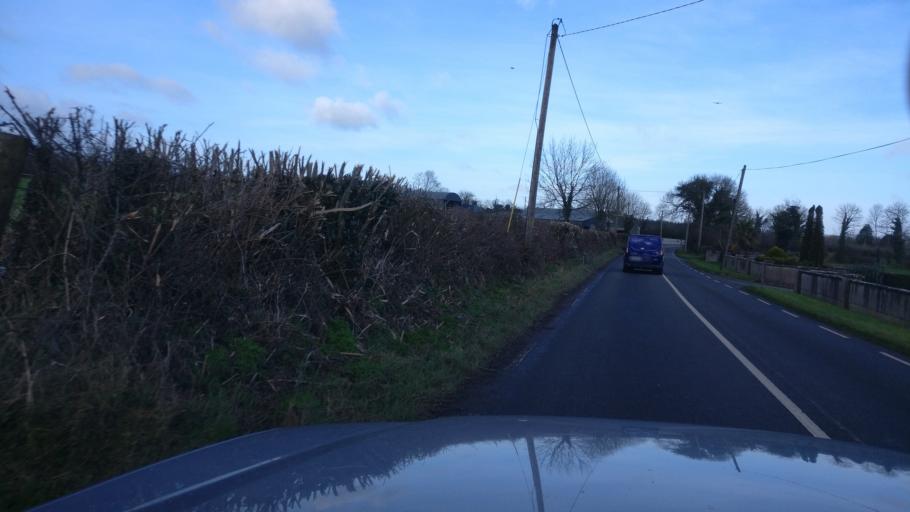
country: IE
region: Leinster
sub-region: Kilkenny
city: Castlecomer
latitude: 52.8415
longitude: -7.1859
